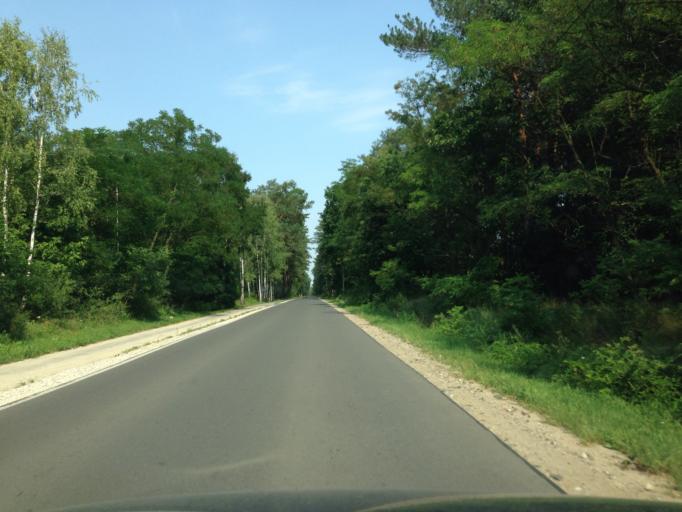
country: PL
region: Kujawsko-Pomorskie
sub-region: Powiat golubsko-dobrzynski
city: Golub-Dobrzyn
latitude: 53.0819
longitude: 19.0316
